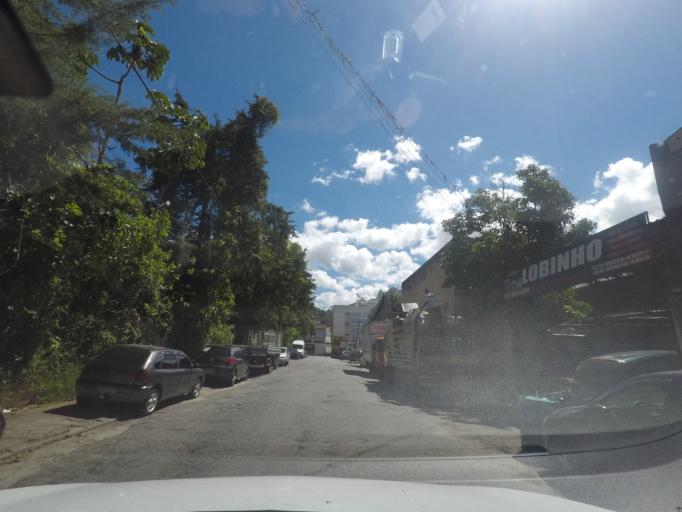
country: BR
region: Rio de Janeiro
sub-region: Teresopolis
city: Teresopolis
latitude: -22.4204
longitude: -42.9737
